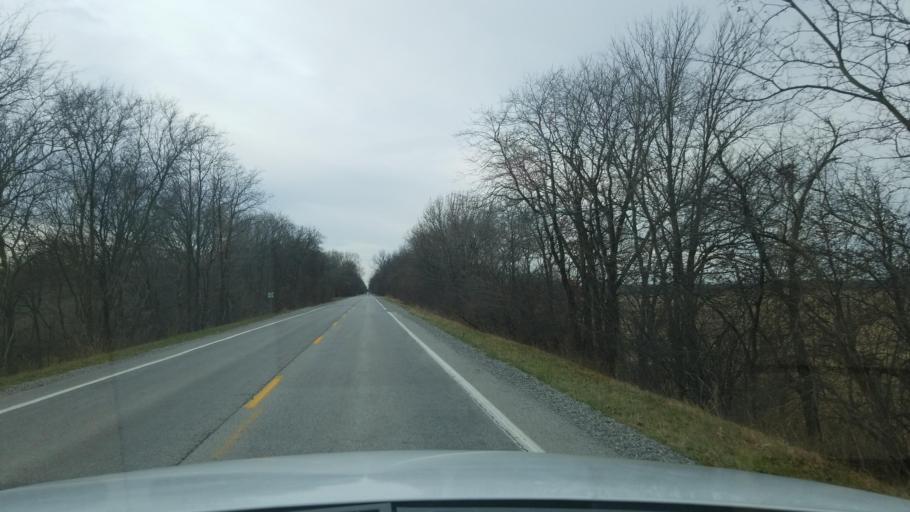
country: US
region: Illinois
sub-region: White County
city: Carmi
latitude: 37.9312
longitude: -88.0900
